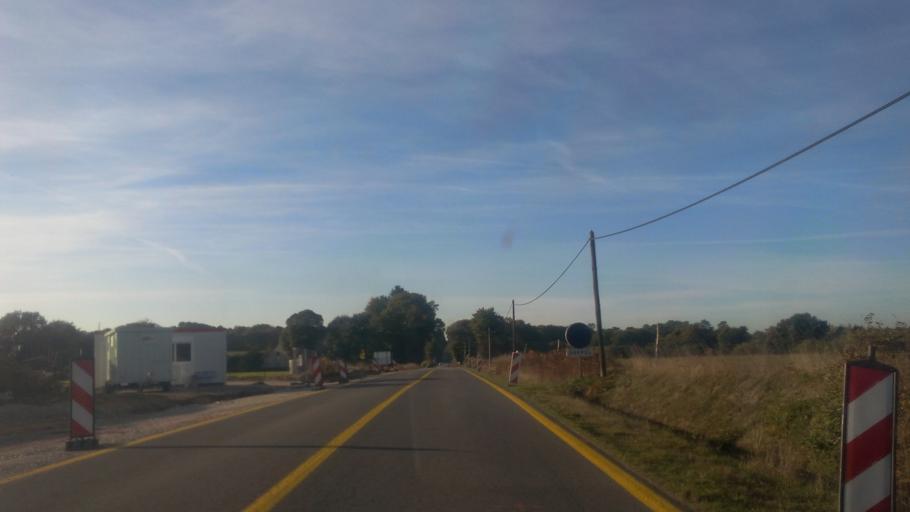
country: FR
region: Brittany
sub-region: Departement du Morbihan
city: La Vraie-Croix
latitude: 47.6974
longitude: -2.5353
